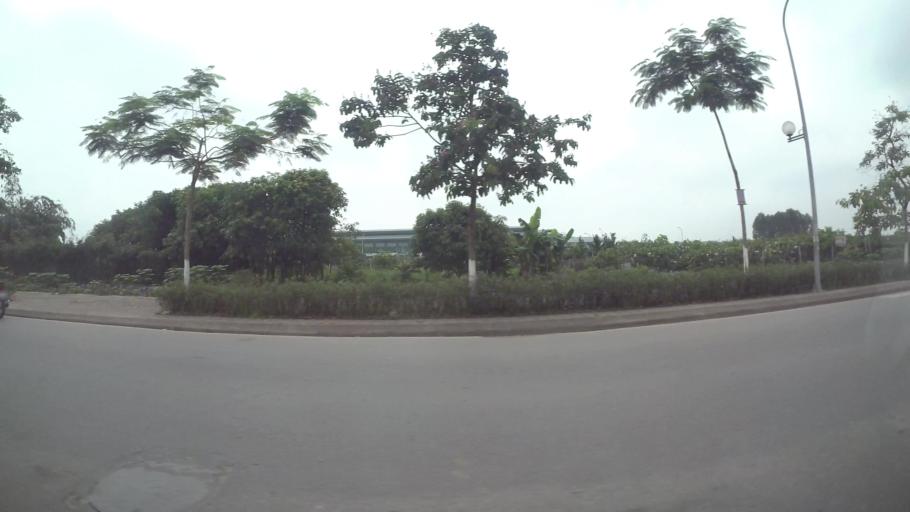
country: VN
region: Ha Noi
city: Trau Quy
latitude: 21.0433
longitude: 105.9254
